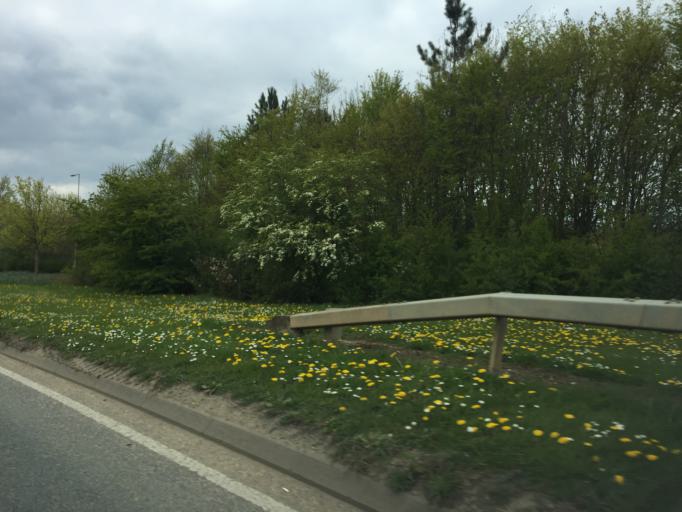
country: GB
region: England
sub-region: Milton Keynes
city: Broughton
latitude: 52.0429
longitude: -0.7170
